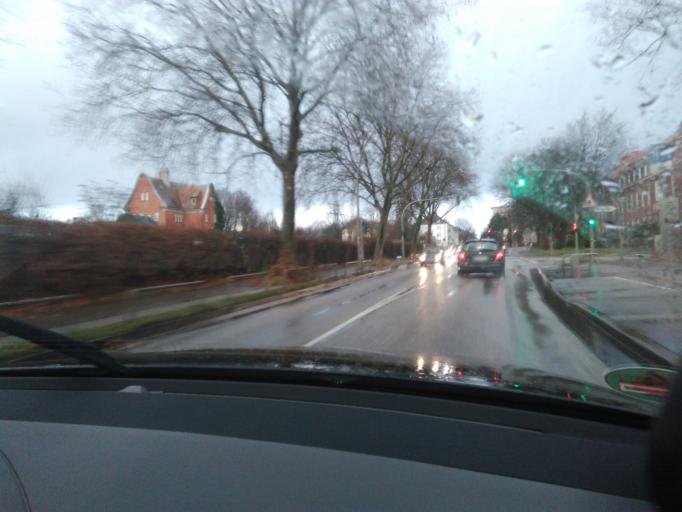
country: DE
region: Hamburg
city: Barmbek-Nord
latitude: 53.6058
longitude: 10.0344
